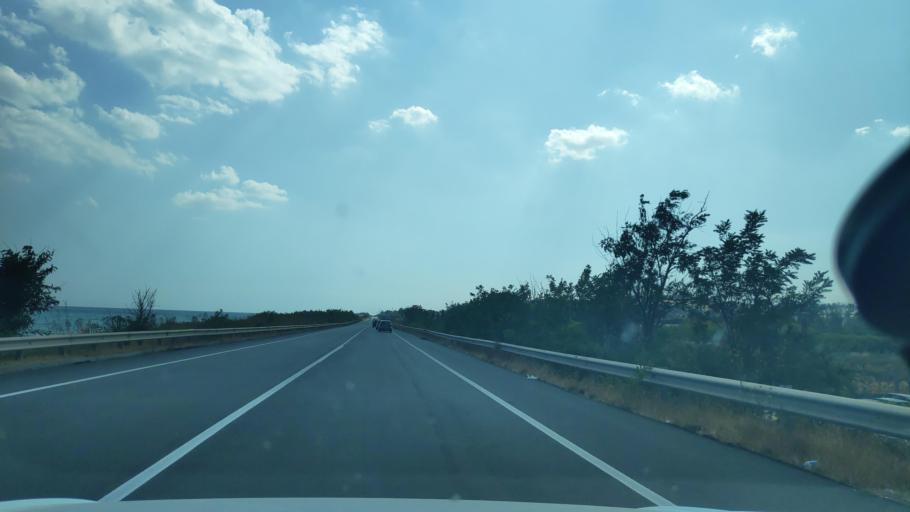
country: IT
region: Calabria
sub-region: Provincia di Reggio Calabria
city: Monasterace Marina
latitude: 38.4246
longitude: 16.5673
